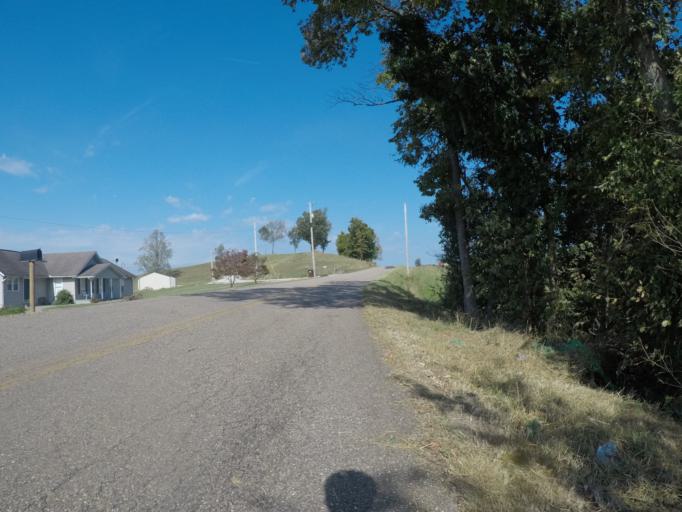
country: US
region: West Virginia
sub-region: Cabell County
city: Lesage
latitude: 38.6458
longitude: -82.4170
